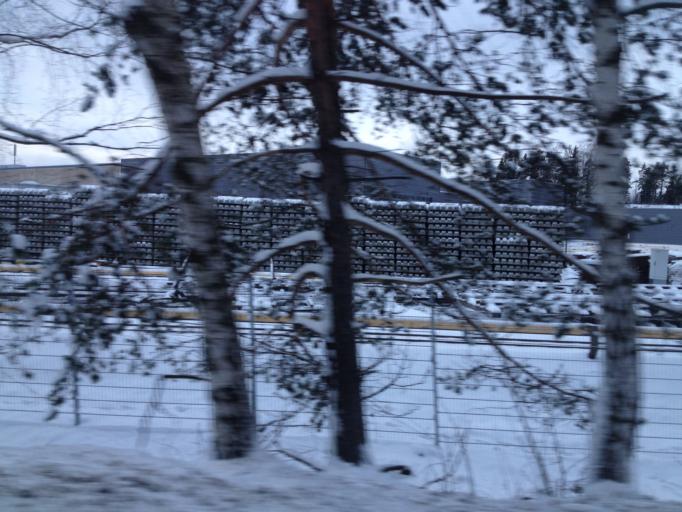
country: FI
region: Uusimaa
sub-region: Helsinki
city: Vantaa
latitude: 60.2143
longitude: 25.0672
